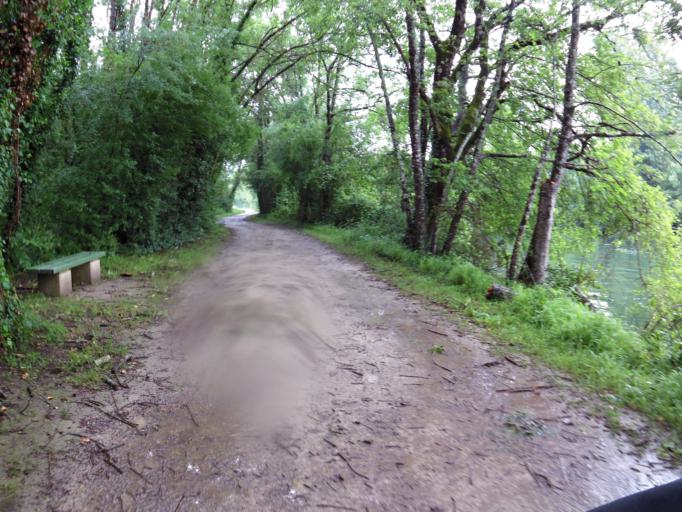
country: FR
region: Poitou-Charentes
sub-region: Departement de la Charente
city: Gond-Pontouvre
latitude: 45.6741
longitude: 0.1538
